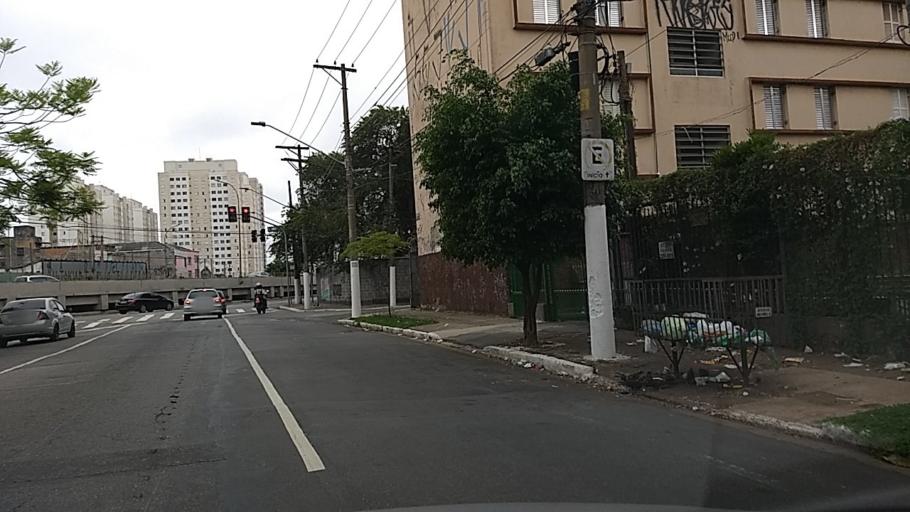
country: BR
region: Sao Paulo
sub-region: Sao Paulo
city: Sao Paulo
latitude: -23.5564
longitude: -46.6231
